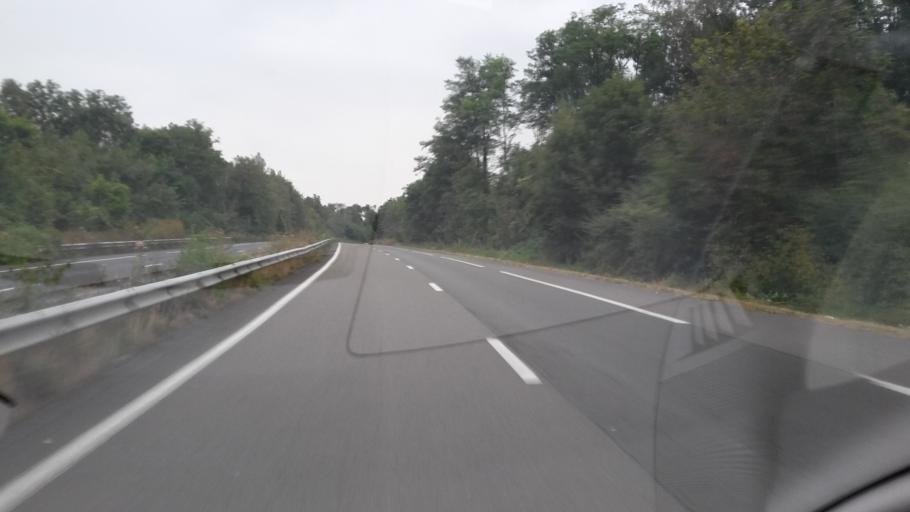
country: FR
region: Champagne-Ardenne
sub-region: Departement des Ardennes
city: Douzy
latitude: 49.7209
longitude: 5.0146
